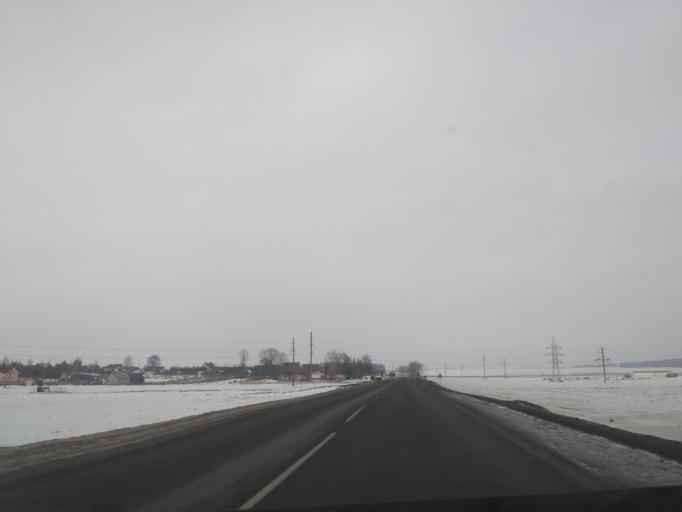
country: BY
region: Minsk
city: Horad Smalyavichy
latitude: 54.0292
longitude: 28.0610
